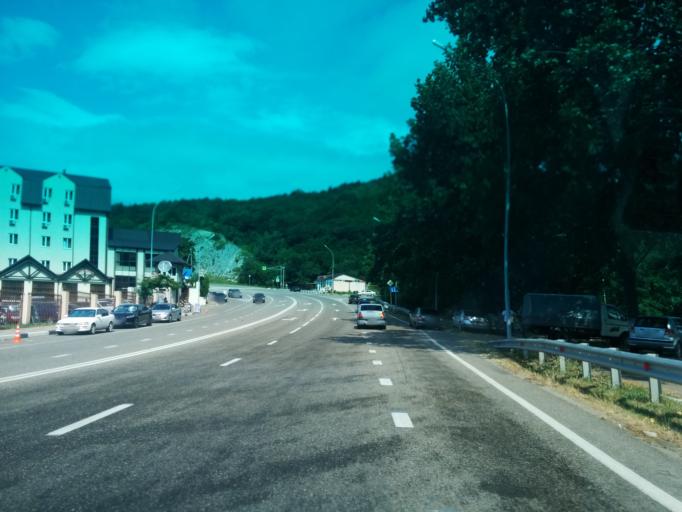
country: RU
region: Krasnodarskiy
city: Nebug
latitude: 44.1656
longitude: 38.9998
